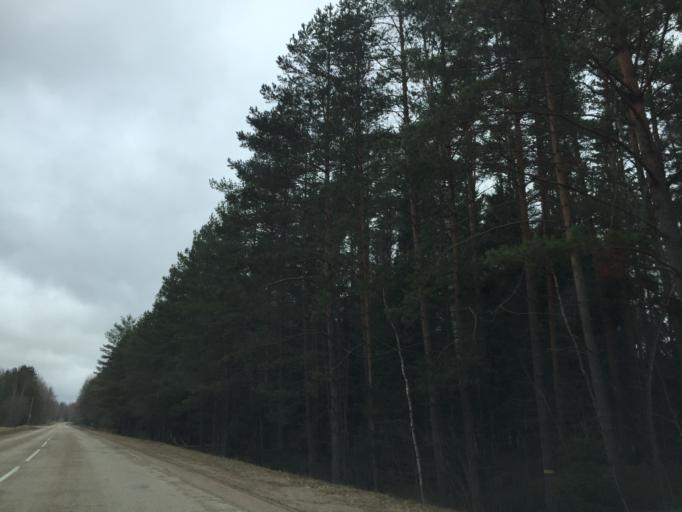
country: LV
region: Ilukste
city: Ilukste
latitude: 55.9614
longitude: 26.3033
